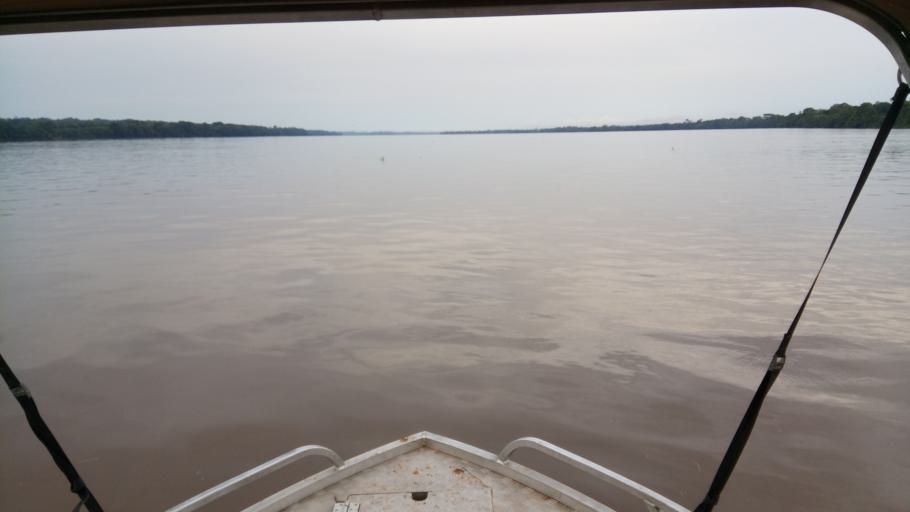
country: CD
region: Eastern Province
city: Kisangani
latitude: 0.5725
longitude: 24.8477
